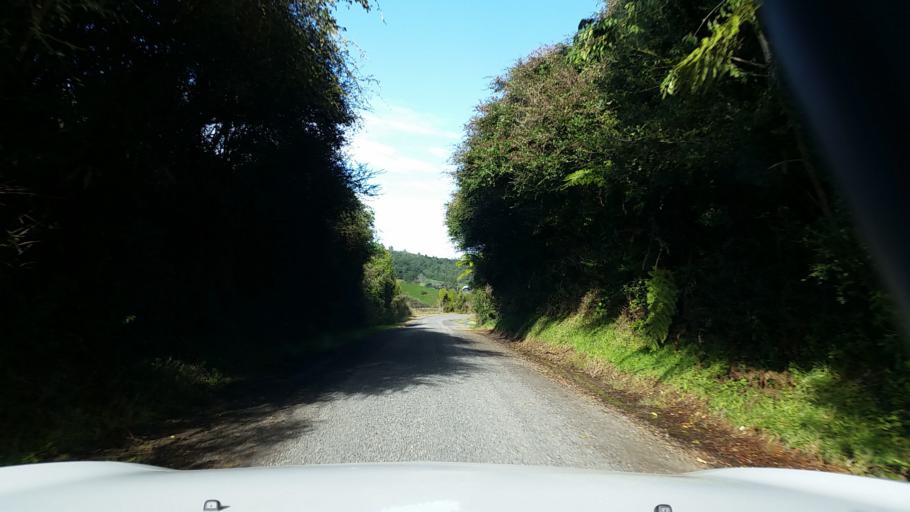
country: NZ
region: Waikato
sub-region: Matamata-Piako District
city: Matamata
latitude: -37.8143
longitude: 175.6343
